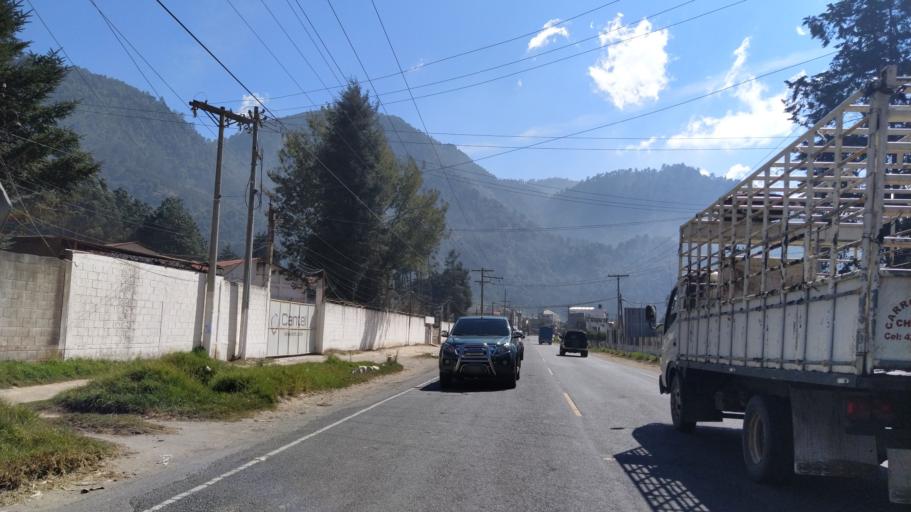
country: GT
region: Quetzaltenango
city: Cantel
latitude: 14.8107
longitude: -91.4480
